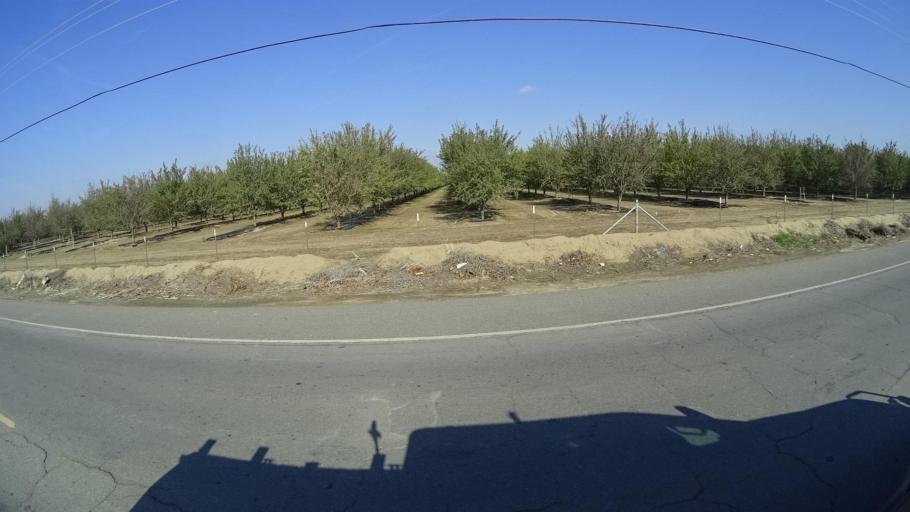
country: US
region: California
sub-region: Kern County
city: Arvin
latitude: 35.1948
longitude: -118.8443
